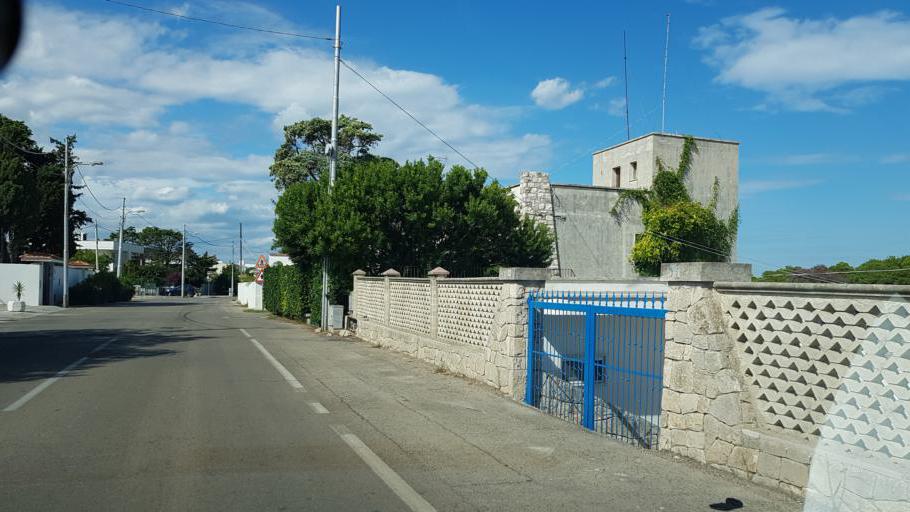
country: IT
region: Apulia
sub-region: Provincia di Lecce
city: Borgagne
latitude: 40.2698
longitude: 18.4299
